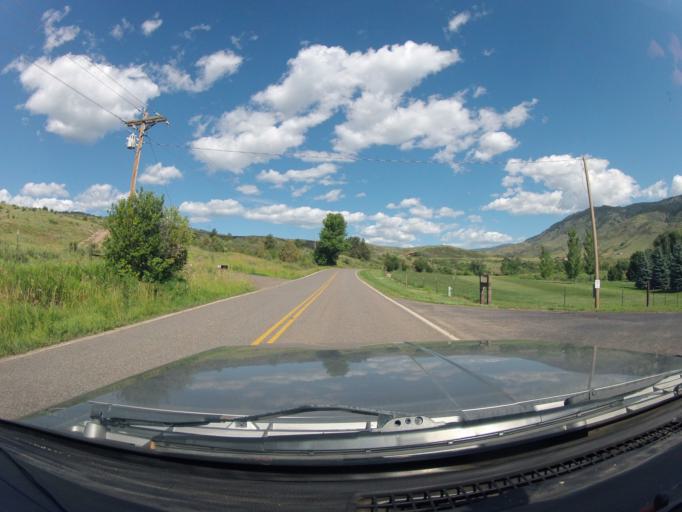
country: US
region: Colorado
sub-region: Larimer County
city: Laporte
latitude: 40.5117
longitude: -105.2504
